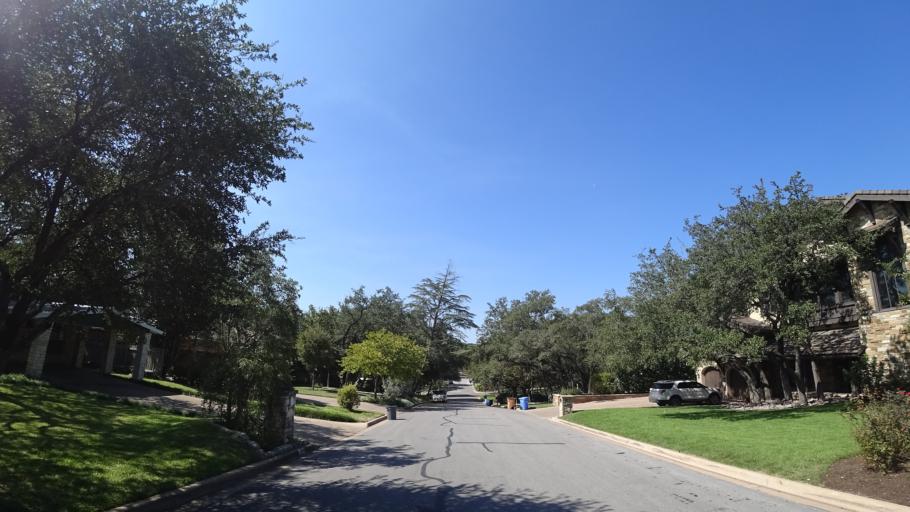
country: US
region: Texas
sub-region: Travis County
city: Rollingwood
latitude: 30.2736
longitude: -97.7879
